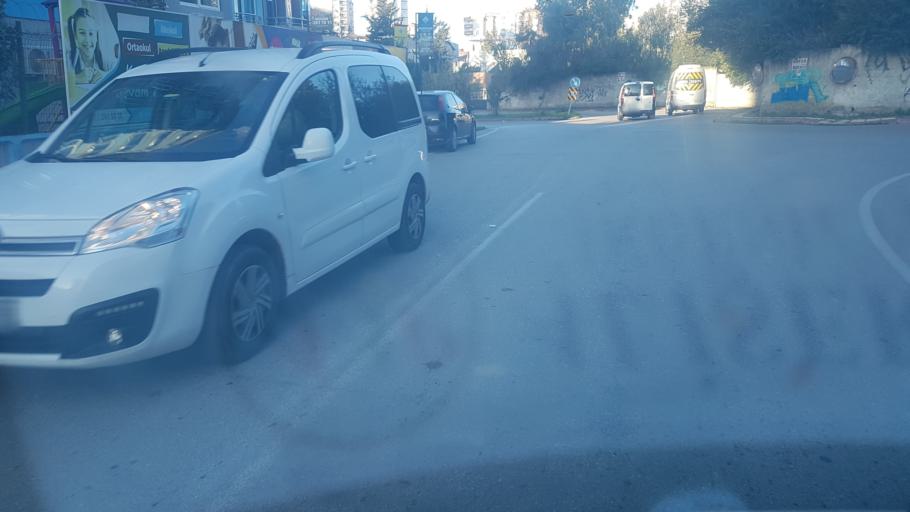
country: TR
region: Adana
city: Seyhan
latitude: 37.0249
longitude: 35.2726
